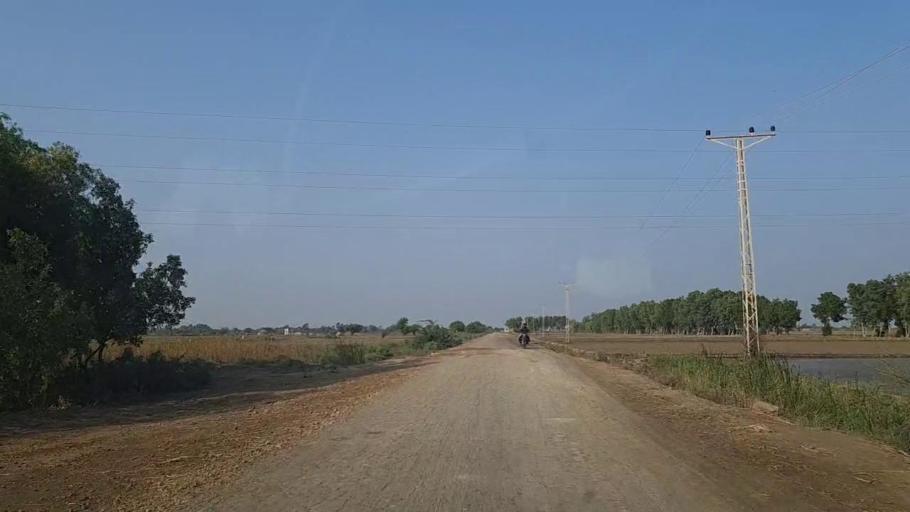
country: PK
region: Sindh
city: Mirpur Sakro
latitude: 24.5635
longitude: 67.6699
